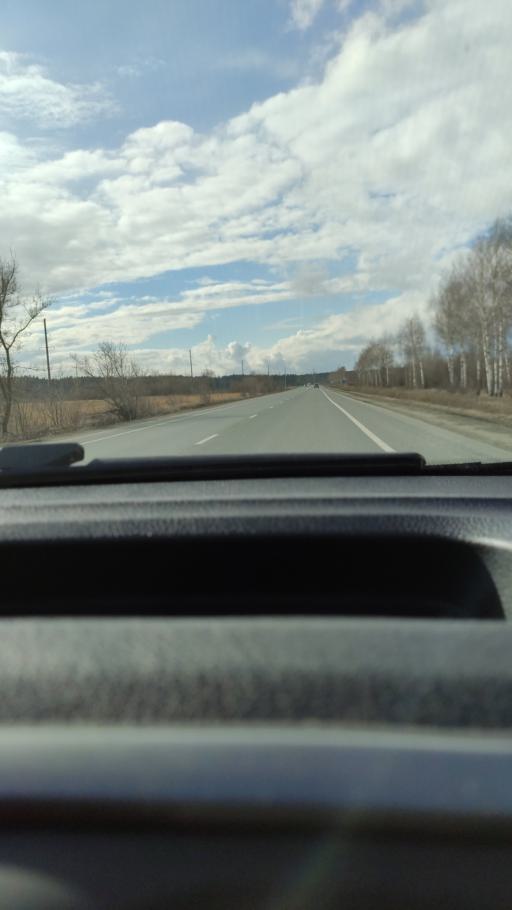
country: RU
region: Samara
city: Kurumoch
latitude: 53.4892
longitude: 49.9903
